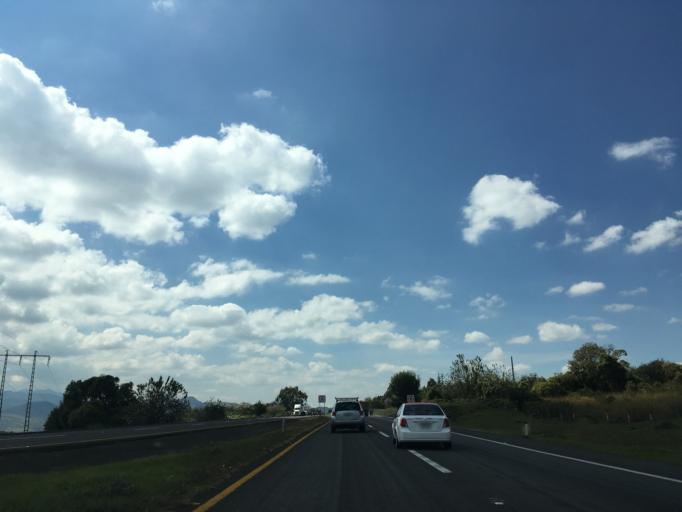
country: MX
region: Michoacan
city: Acuitzio del Canje
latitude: 19.5534
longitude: -101.3540
